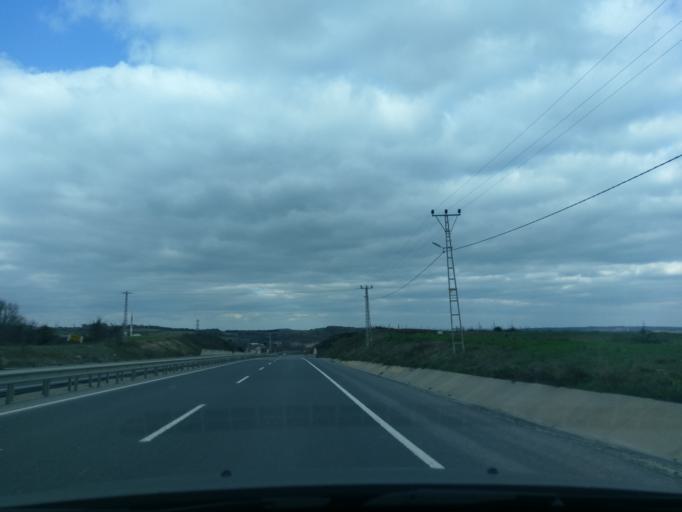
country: TR
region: Istanbul
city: Durusu
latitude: 41.2712
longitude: 28.6671
